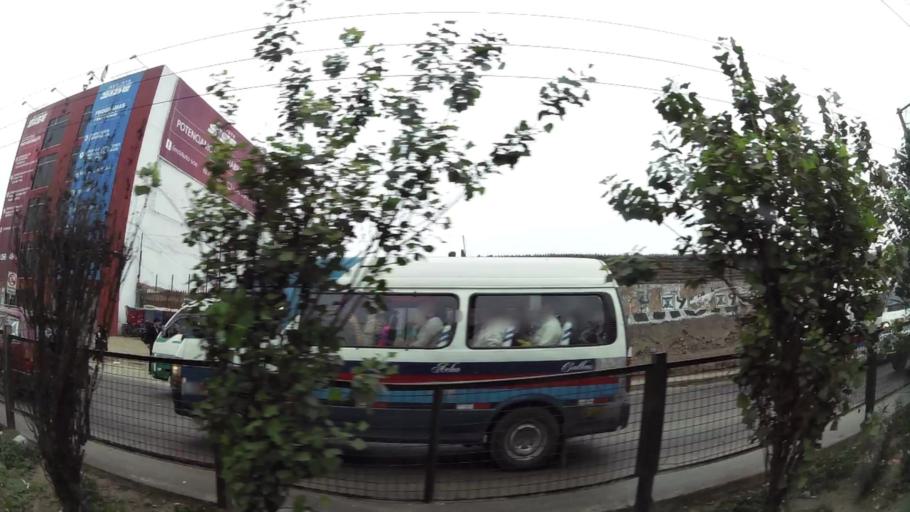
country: PE
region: Lima
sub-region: Lima
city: Santa Maria
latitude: -12.0199
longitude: -76.9013
